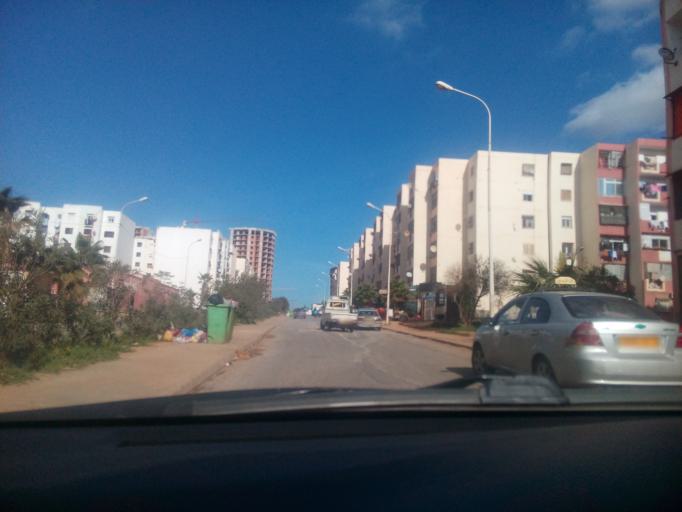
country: DZ
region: Oran
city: Bir el Djir
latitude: 35.7058
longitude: -0.5635
